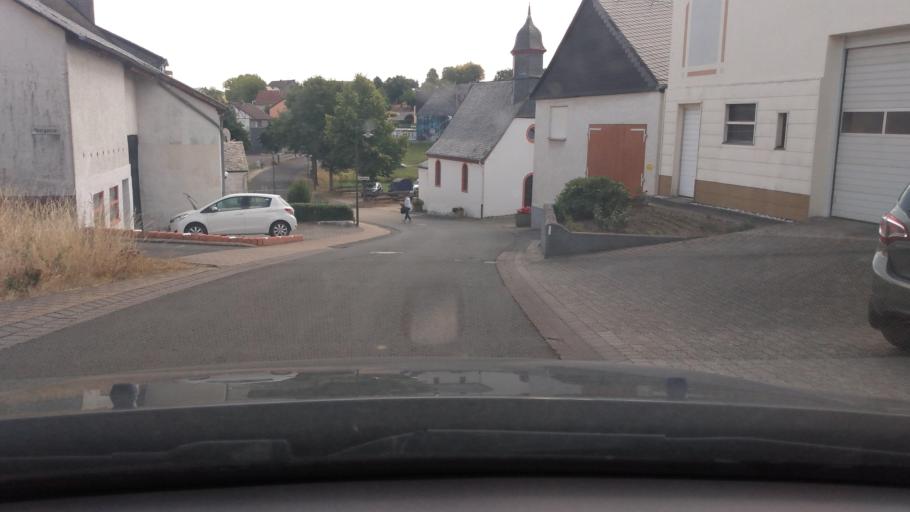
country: DE
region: Rheinland-Pfalz
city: Kommen
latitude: 49.8792
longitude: 7.1295
